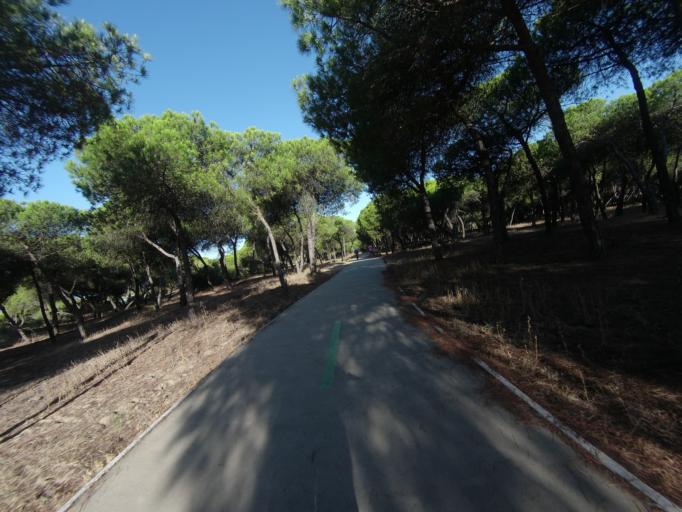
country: ES
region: Andalusia
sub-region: Provincia de Huelva
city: Aljaraque
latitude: 37.2061
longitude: -7.0292
